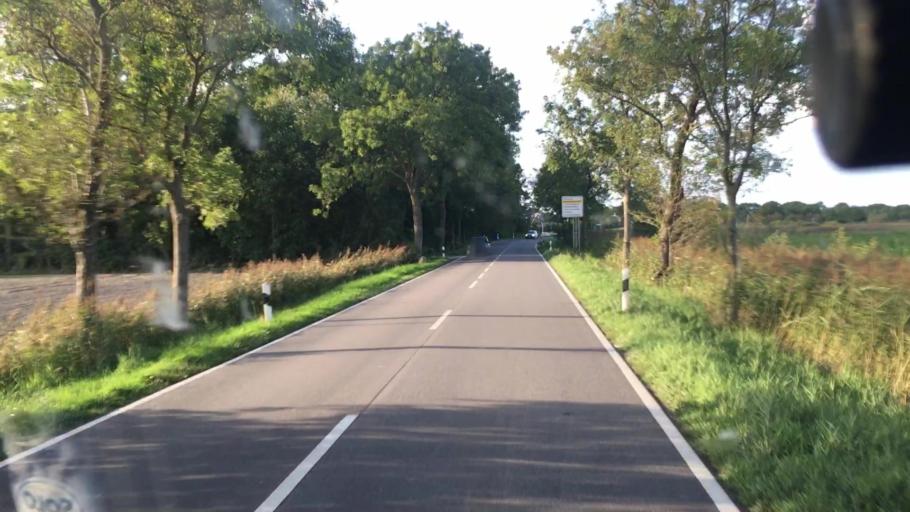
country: DE
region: Lower Saxony
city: Neuharlingersiel
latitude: 53.6876
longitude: 7.6866
